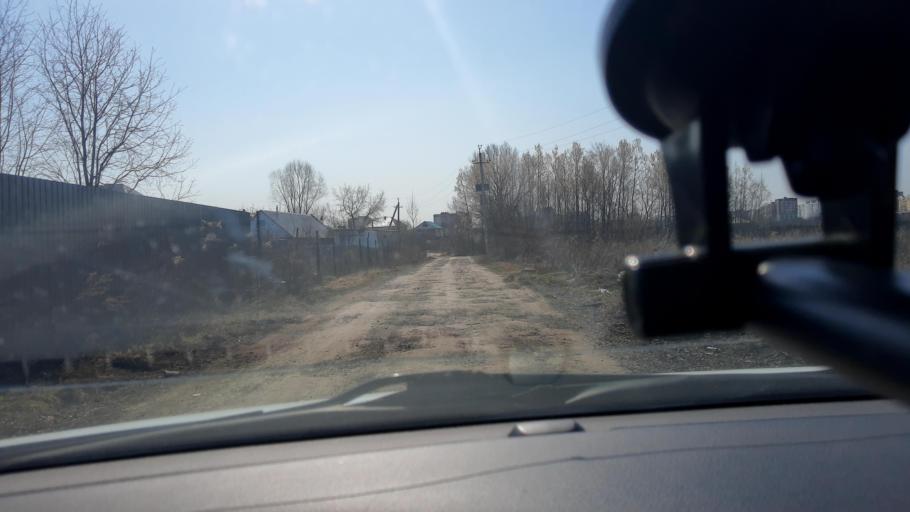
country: RU
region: Bashkortostan
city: Mikhaylovka
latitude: 54.7206
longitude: 55.8233
